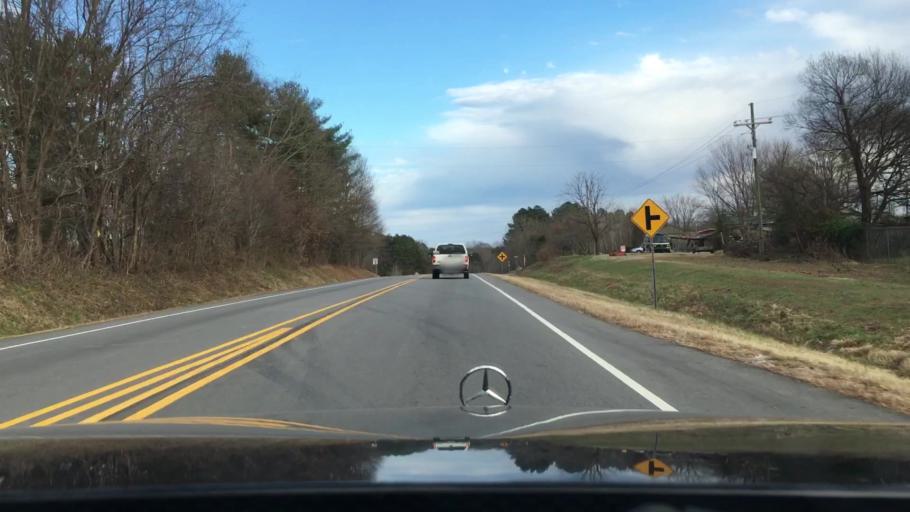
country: US
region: North Carolina
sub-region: Caswell County
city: Yanceyville
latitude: 36.4081
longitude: -79.3313
